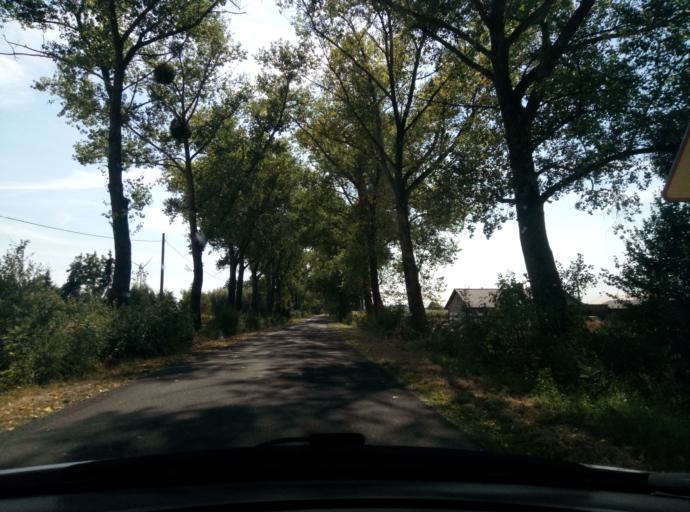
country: PL
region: Kujawsko-Pomorskie
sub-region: Powiat brodnicki
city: Jablonowo Pomorskie
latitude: 53.4008
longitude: 19.2021
